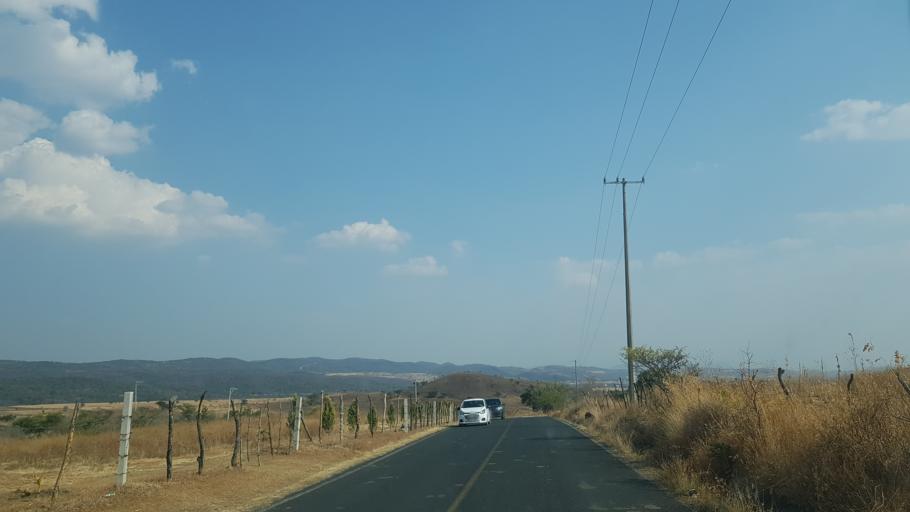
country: MX
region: Morelos
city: Tlacotepec
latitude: 18.8024
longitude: -98.7128
